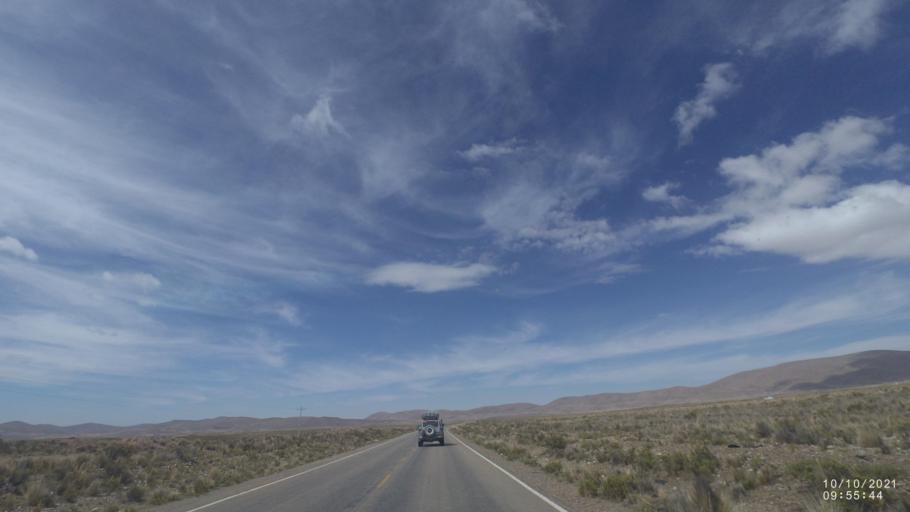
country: BO
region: La Paz
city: Colquiri
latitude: -17.3128
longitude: -67.3688
